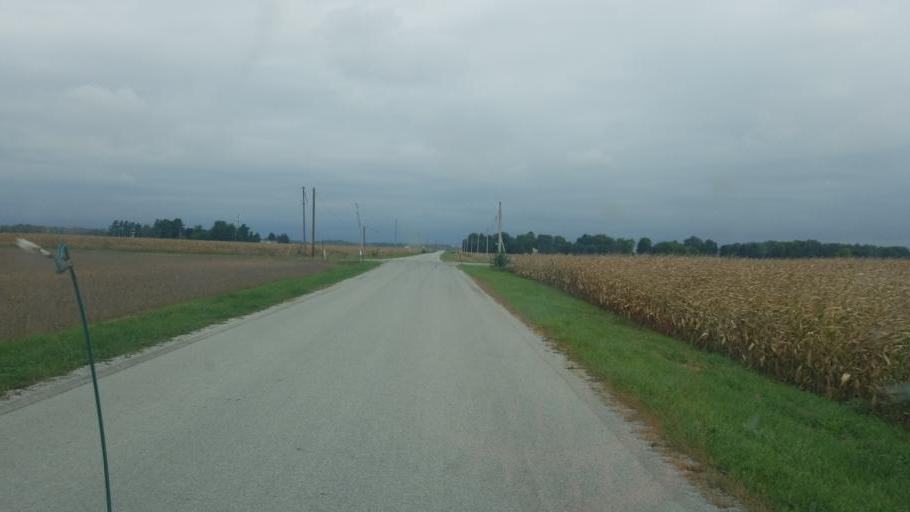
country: US
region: Ohio
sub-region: Wood County
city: Bowling Green
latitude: 41.3261
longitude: -83.6700
